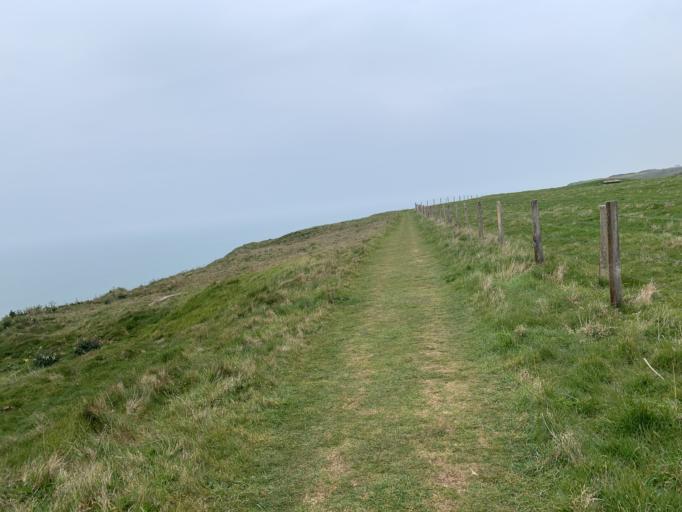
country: FR
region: Haute-Normandie
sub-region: Departement de la Seine-Maritime
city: Saint-Jouin-Bruneval
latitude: 49.6859
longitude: 0.1645
